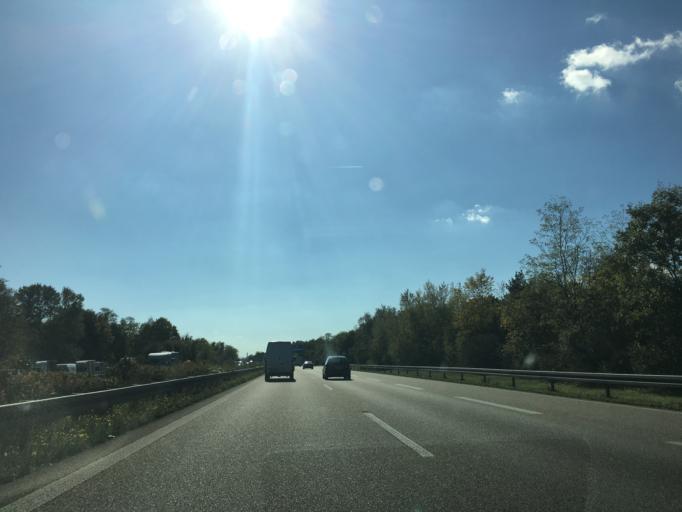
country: FR
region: Alsace
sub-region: Departement du Haut-Rhin
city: Chalampe
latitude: 47.7915
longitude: 7.5389
